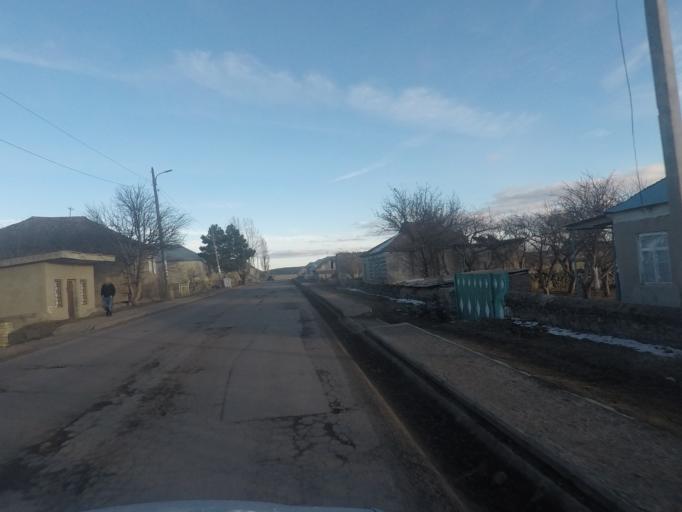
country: GE
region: Kvemo Kartli
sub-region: Tsalka
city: Tsalka
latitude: 41.6028
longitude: 44.0506
